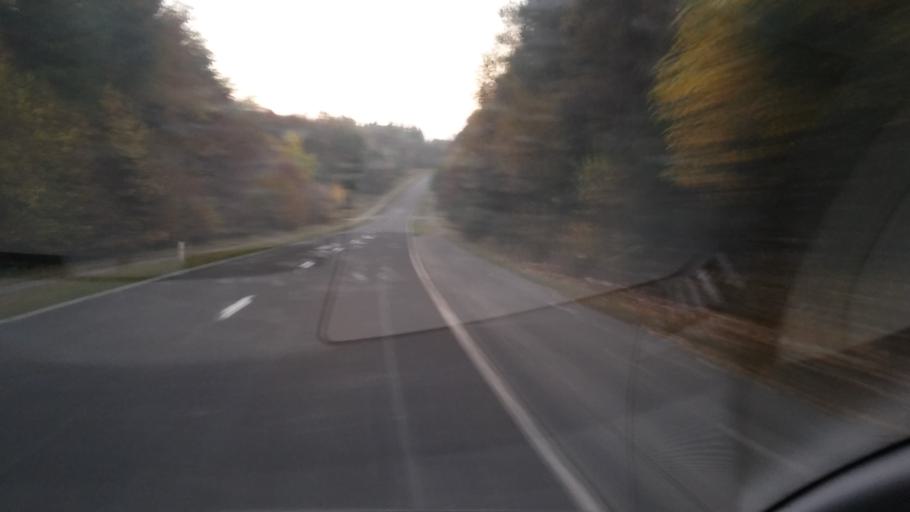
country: BE
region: Wallonia
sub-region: Province du Luxembourg
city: Etalle
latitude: 49.6394
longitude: 5.5676
